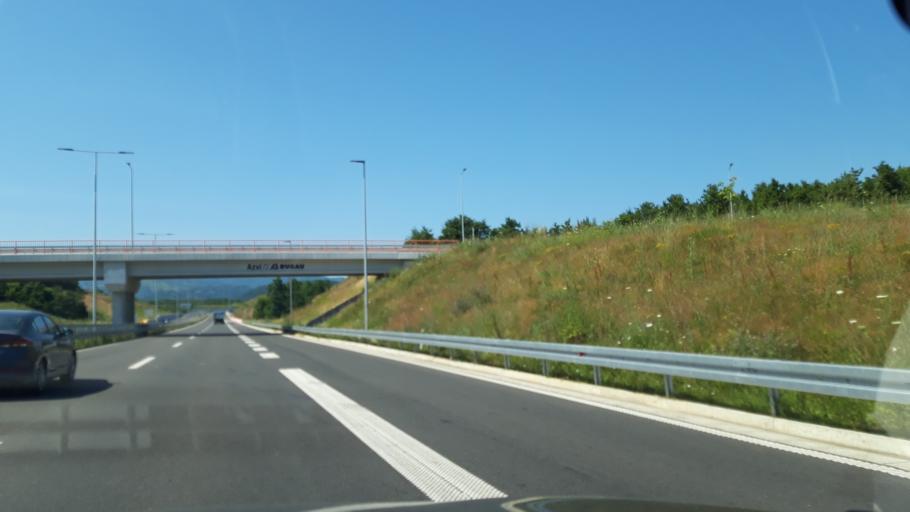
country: RS
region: Central Serbia
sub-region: Pcinjski Okrug
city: Vladicin Han
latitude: 42.7033
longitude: 22.0747
